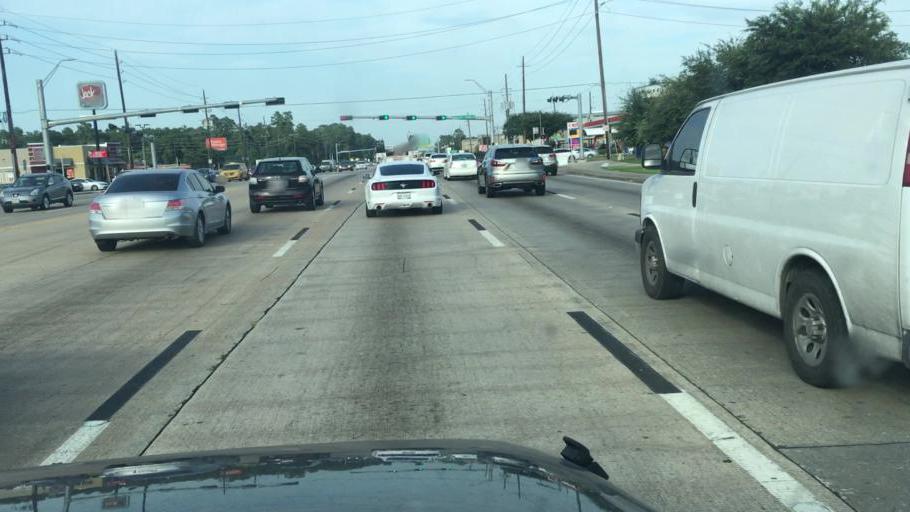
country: US
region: Texas
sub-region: Harris County
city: Spring
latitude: 30.0233
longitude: -95.4215
